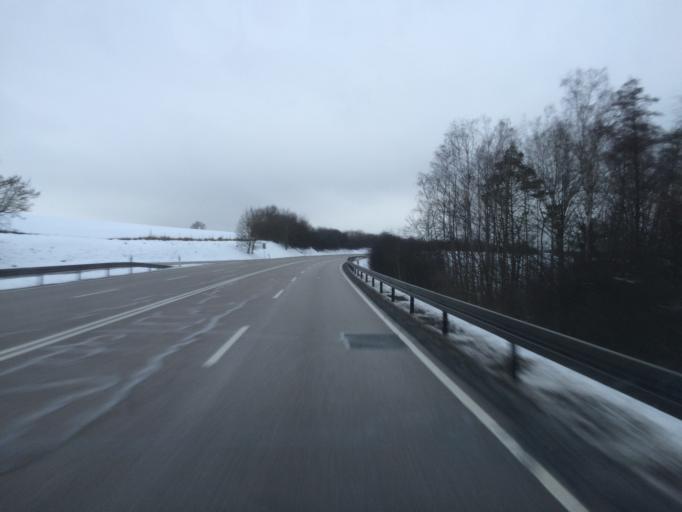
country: DE
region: Bavaria
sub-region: Upper Palatinate
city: Breitenbrunn
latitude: 49.3690
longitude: 12.0401
